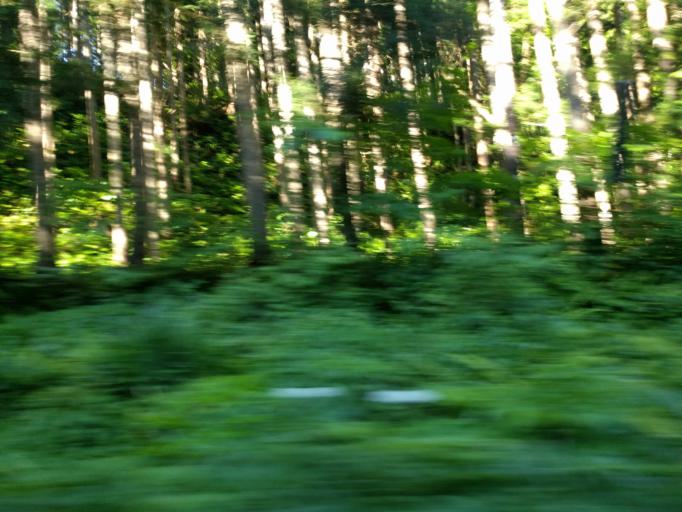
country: JP
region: Fukushima
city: Kitakata
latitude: 37.3470
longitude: 139.8104
